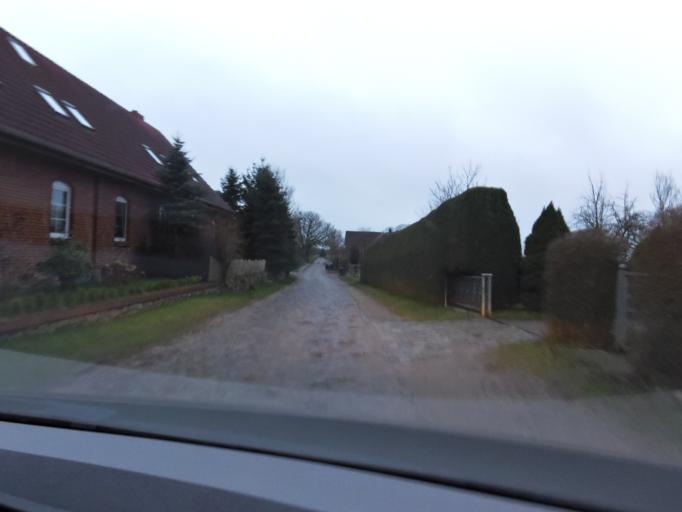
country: DE
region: Mecklenburg-Vorpommern
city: Roggendorf
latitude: 53.6876
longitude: 10.9963
